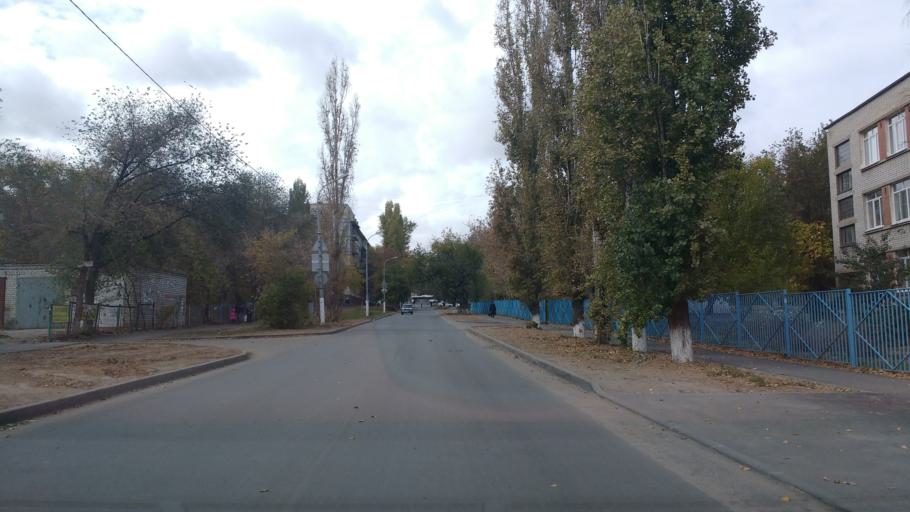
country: RU
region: Volgograd
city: Vodstroy
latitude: 48.7724
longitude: 44.5527
